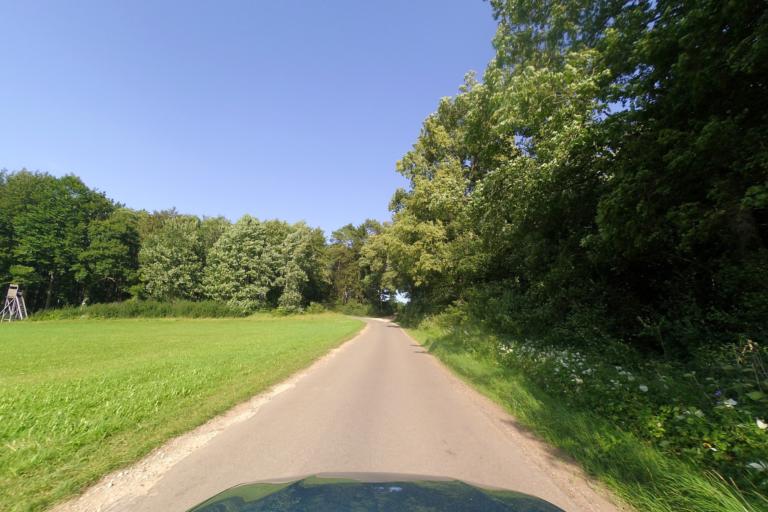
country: DE
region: Baden-Wuerttemberg
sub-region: Regierungsbezirk Stuttgart
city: Hermaringen
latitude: 48.5834
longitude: 10.2631
